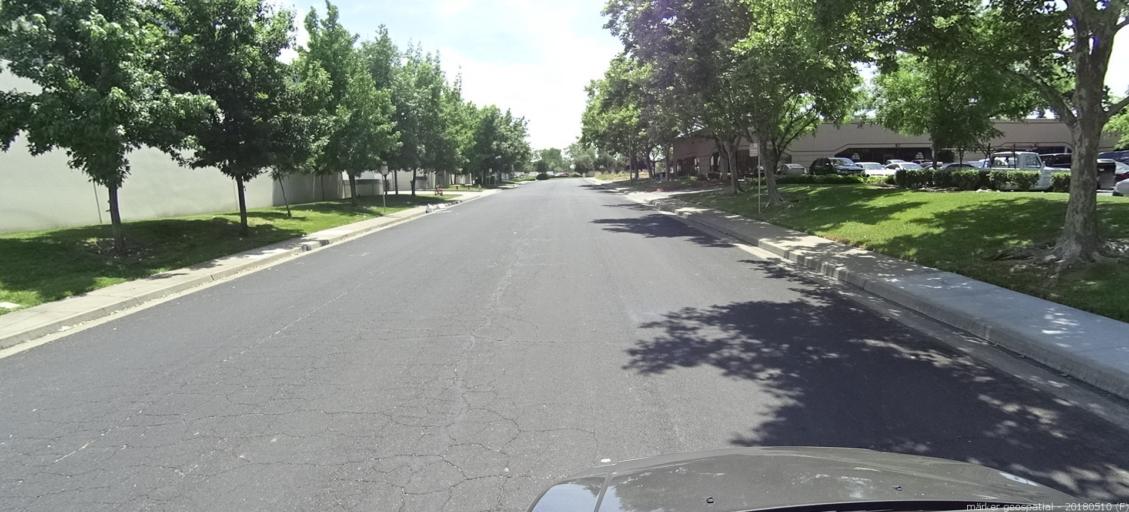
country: US
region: California
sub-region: Sacramento County
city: Rio Linda
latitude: 38.6401
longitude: -121.4636
